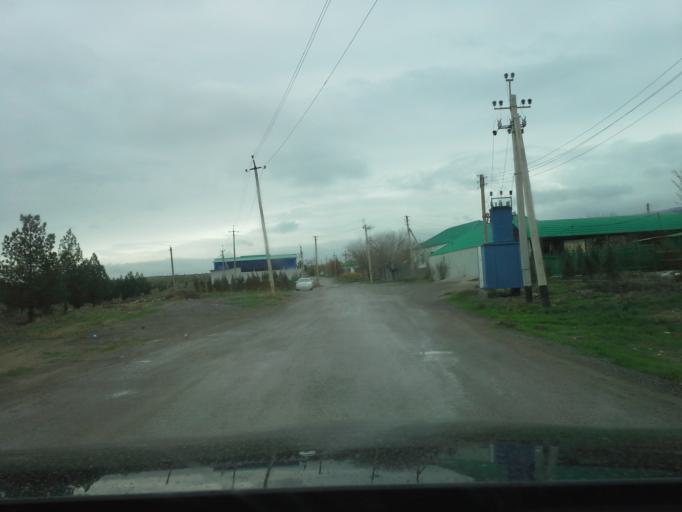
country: TM
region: Ahal
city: Abadan
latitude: 37.9659
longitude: 58.2291
